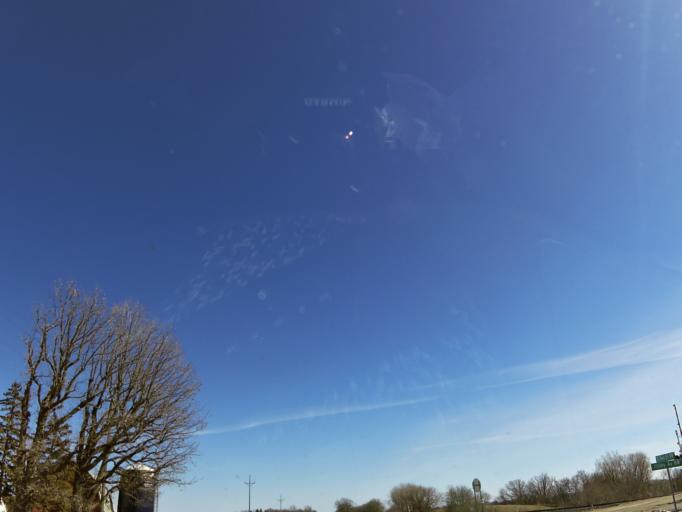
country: US
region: Minnesota
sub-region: Wright County
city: Maple Lake
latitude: 45.2410
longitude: -94.0562
